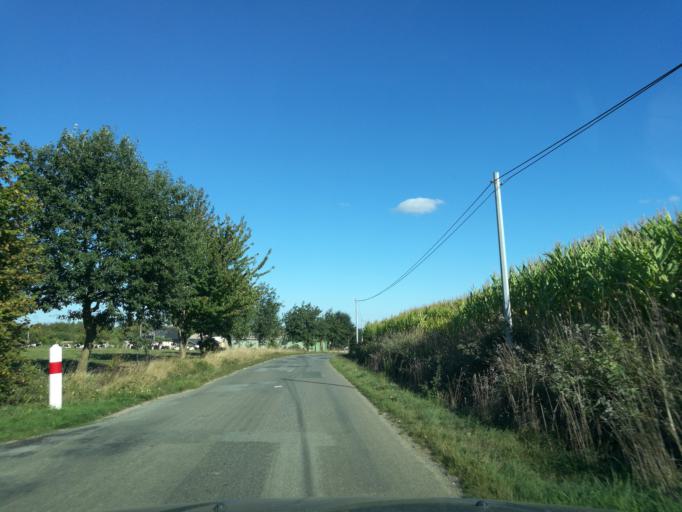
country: FR
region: Brittany
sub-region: Departement d'Ille-et-Vilaine
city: Montauban-de-Bretagne
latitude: 48.1713
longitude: -2.0133
